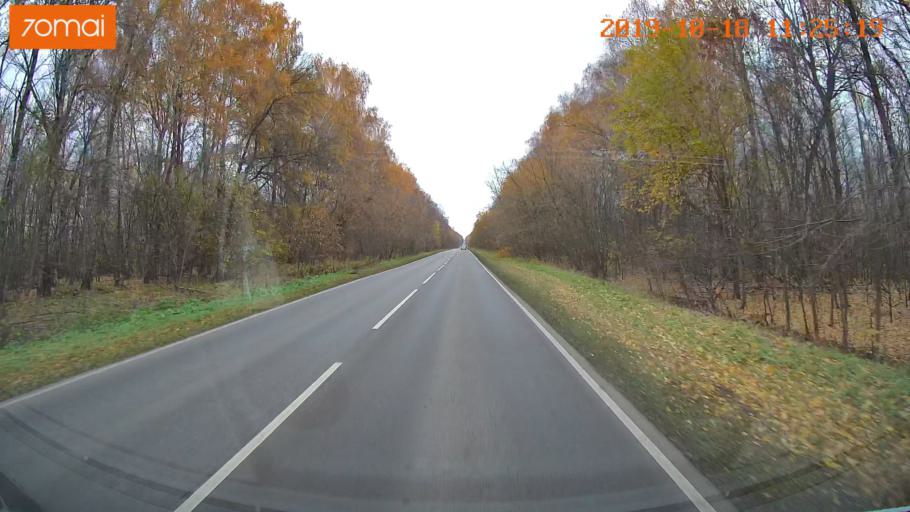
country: RU
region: Tula
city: Kimovsk
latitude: 54.1230
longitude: 38.6159
